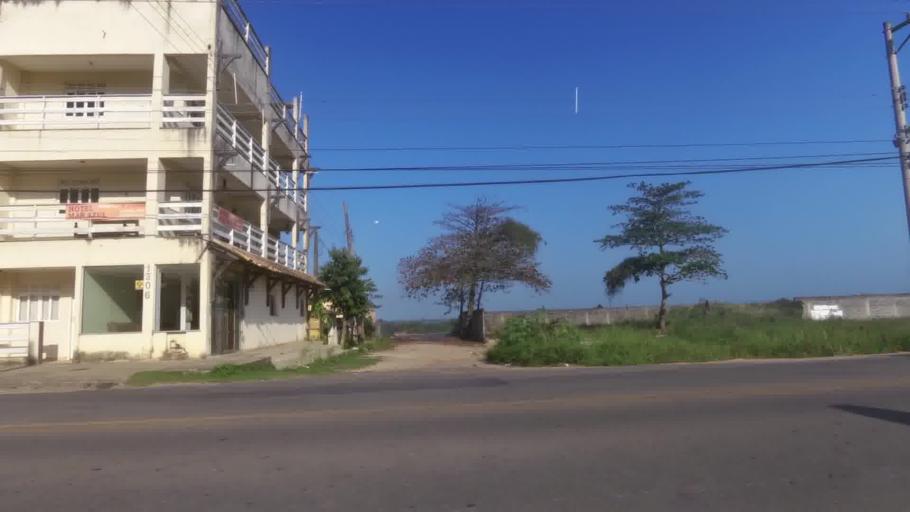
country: BR
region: Espirito Santo
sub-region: Piuma
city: Piuma
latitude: -20.8566
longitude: -40.7538
